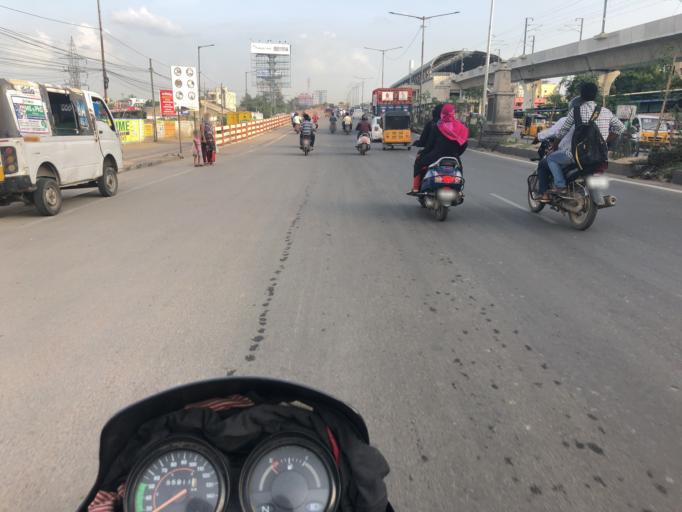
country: IN
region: Telangana
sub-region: Rangareddi
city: Kukatpalli
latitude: 17.4662
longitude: 78.4294
